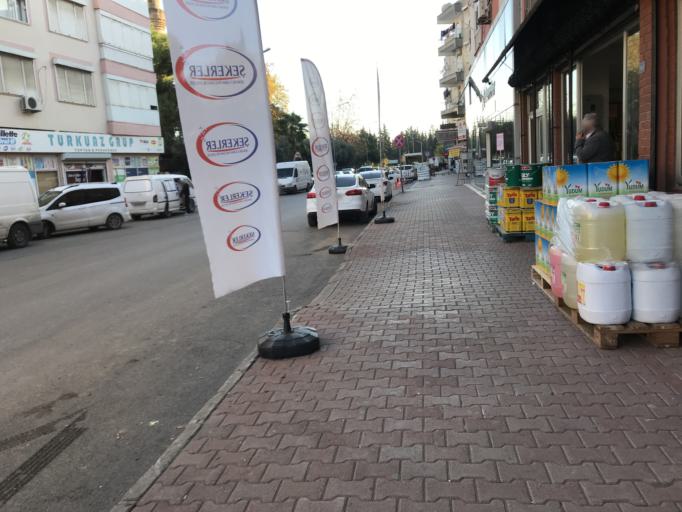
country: TR
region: Antalya
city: Antalya
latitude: 36.8972
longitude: 30.7072
